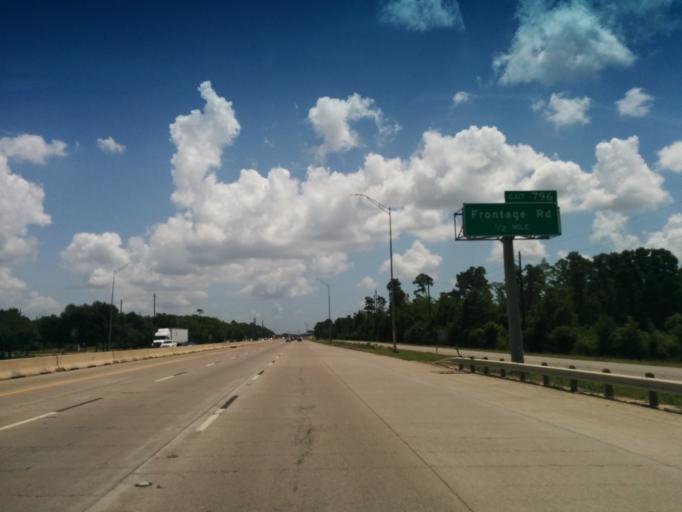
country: US
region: Texas
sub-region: Chambers County
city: Mont Belvieu
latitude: 29.8147
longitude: -94.9335
